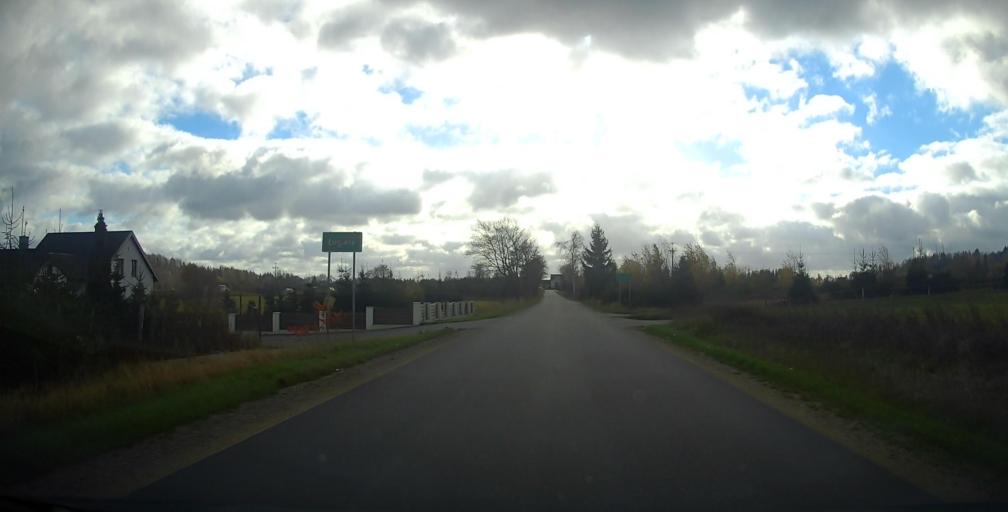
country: PL
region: Podlasie
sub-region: Suwalki
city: Suwalki
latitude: 54.2950
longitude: 22.8789
